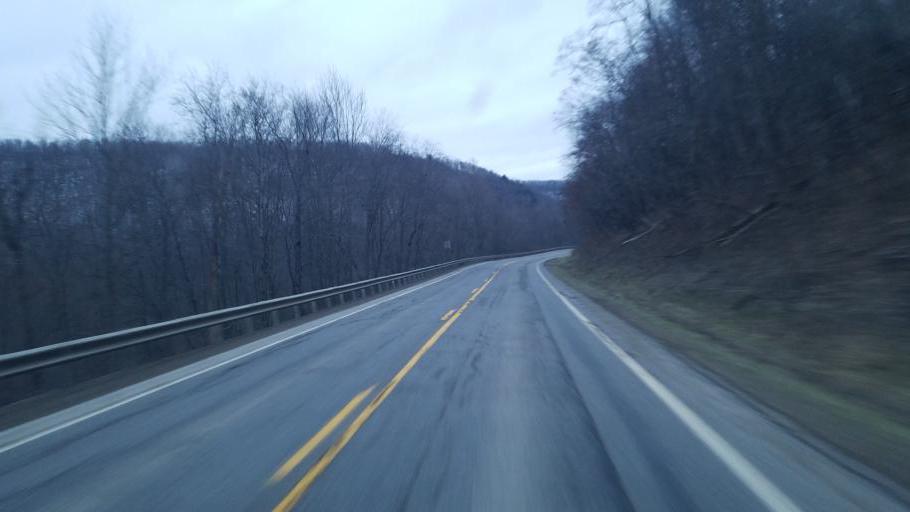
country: US
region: Pennsylvania
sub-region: Potter County
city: Coudersport
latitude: 41.8262
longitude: -77.9565
